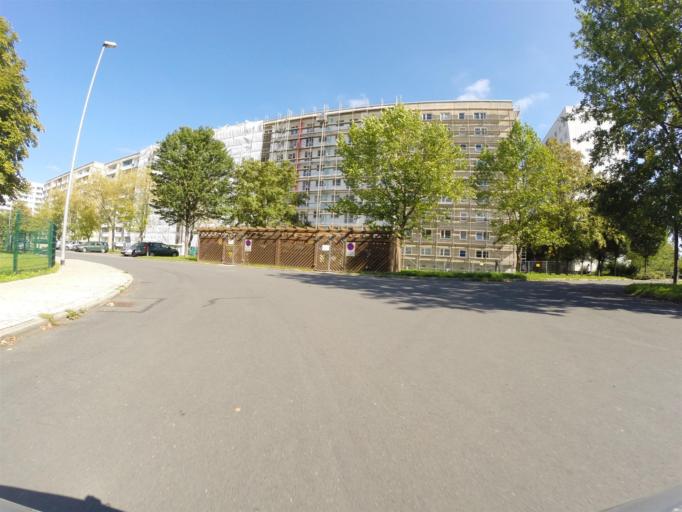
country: DE
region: Thuringia
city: Sulza
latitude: 50.8796
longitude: 11.6037
